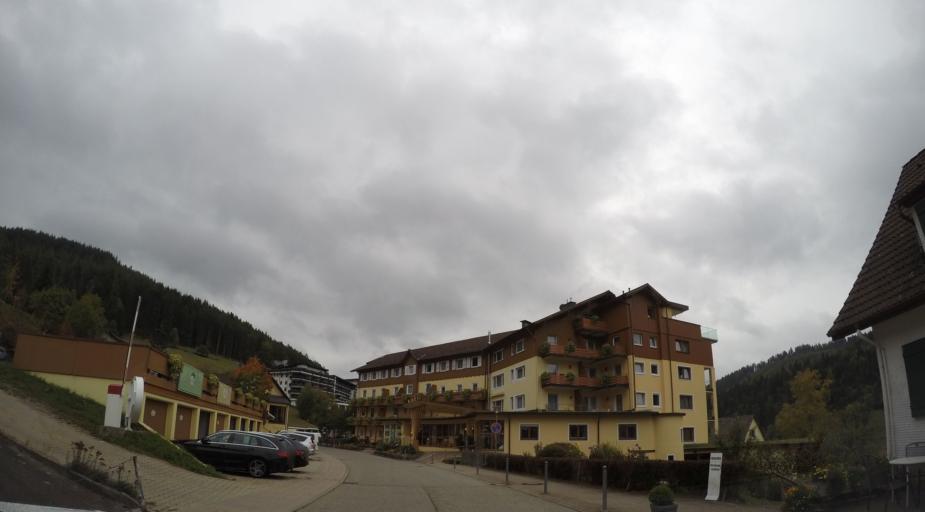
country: DE
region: Baden-Wuerttemberg
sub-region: Karlsruhe Region
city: Baiersbronn
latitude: 48.5387
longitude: 8.3563
